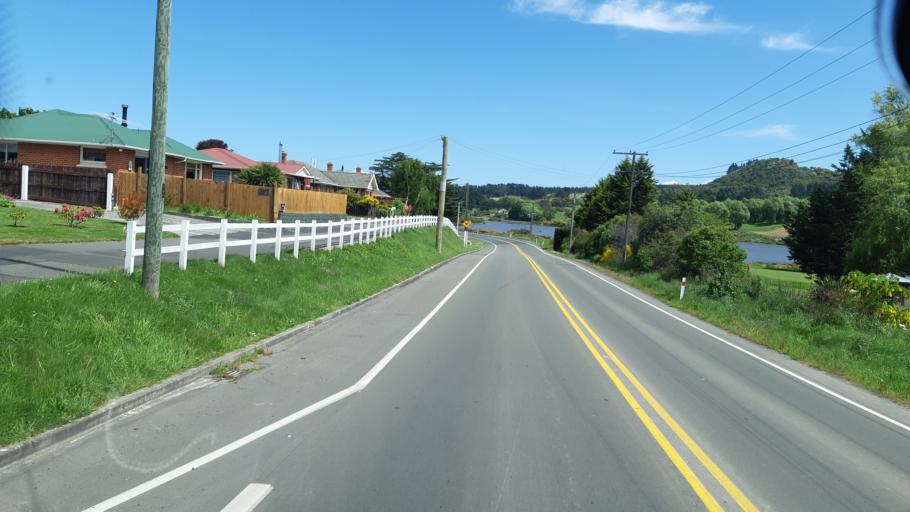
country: NZ
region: Otago
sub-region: Dunedin City
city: Dunedin
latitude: -45.9228
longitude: 170.4038
